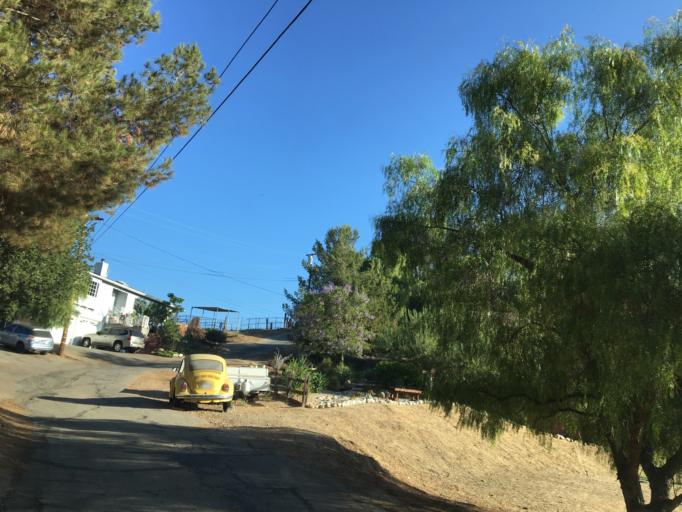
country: US
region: California
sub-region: Los Angeles County
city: San Fernando
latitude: 34.2880
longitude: -118.3739
